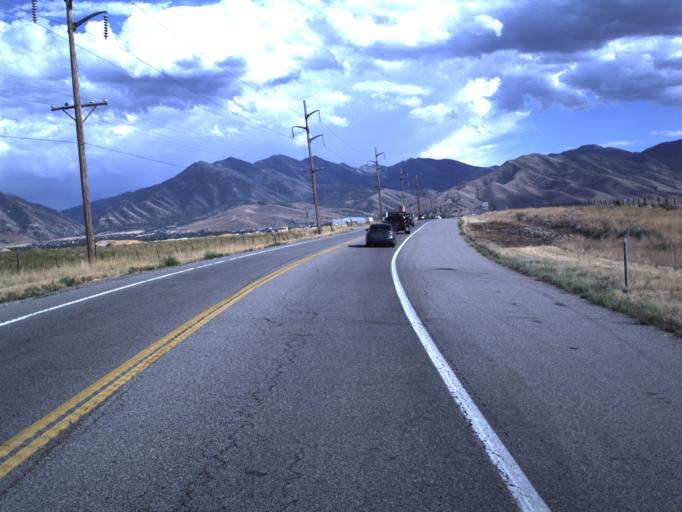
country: US
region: Utah
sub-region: Tooele County
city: Tooele
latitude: 40.5603
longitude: -112.3533
